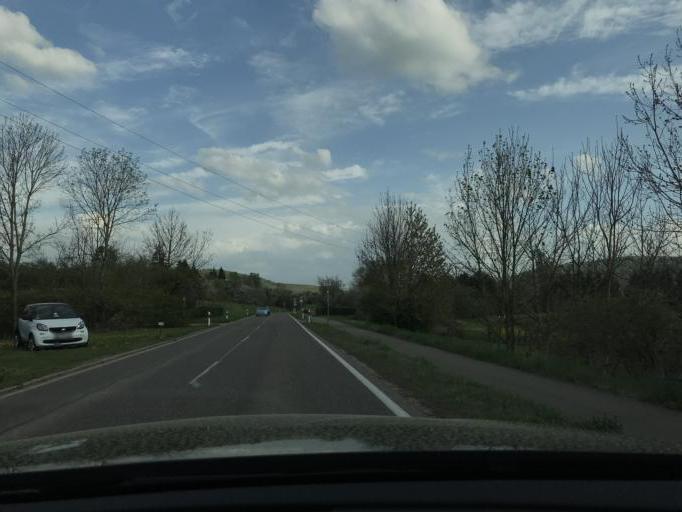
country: DE
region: Baden-Wuerttemberg
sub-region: Regierungsbezirk Stuttgart
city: Weinstadt-Endersbach
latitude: 48.8026
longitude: 9.3512
